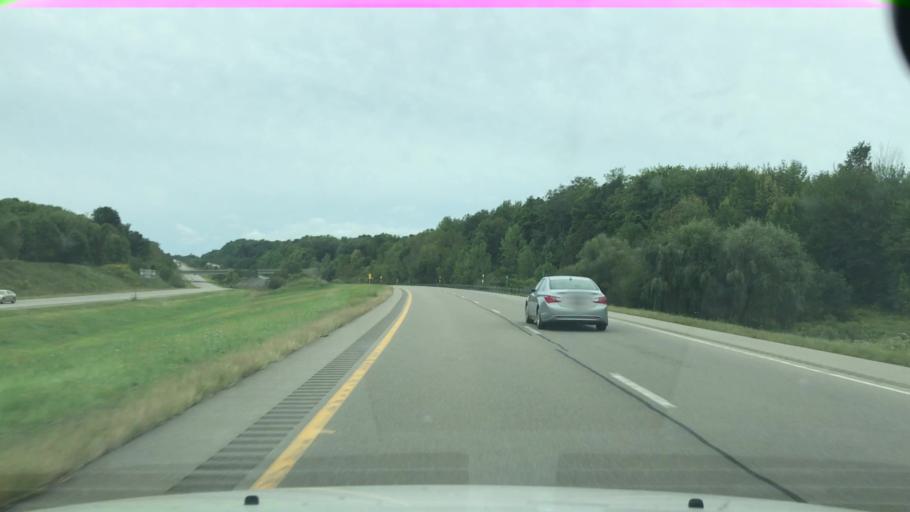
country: US
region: New York
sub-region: Erie County
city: North Boston
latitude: 42.6824
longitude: -78.7874
